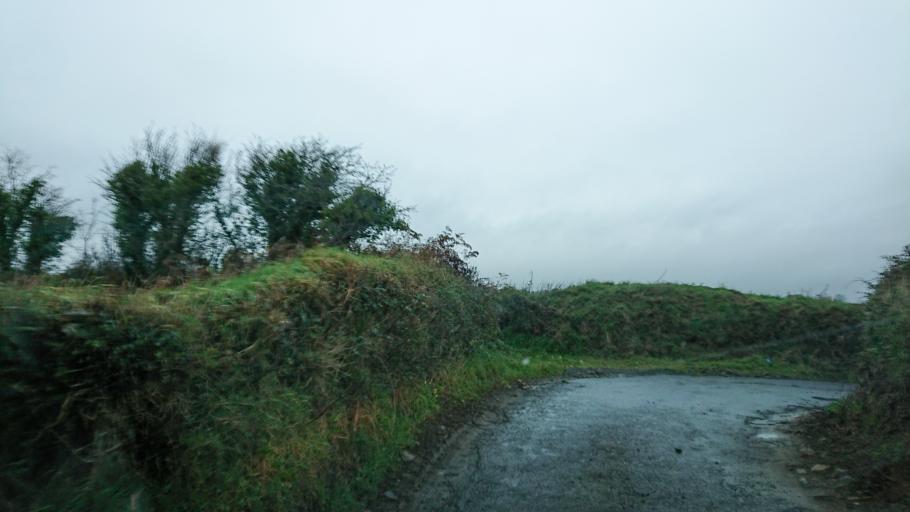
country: IE
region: Munster
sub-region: Waterford
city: Tra Mhor
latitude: 52.1977
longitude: -7.1508
